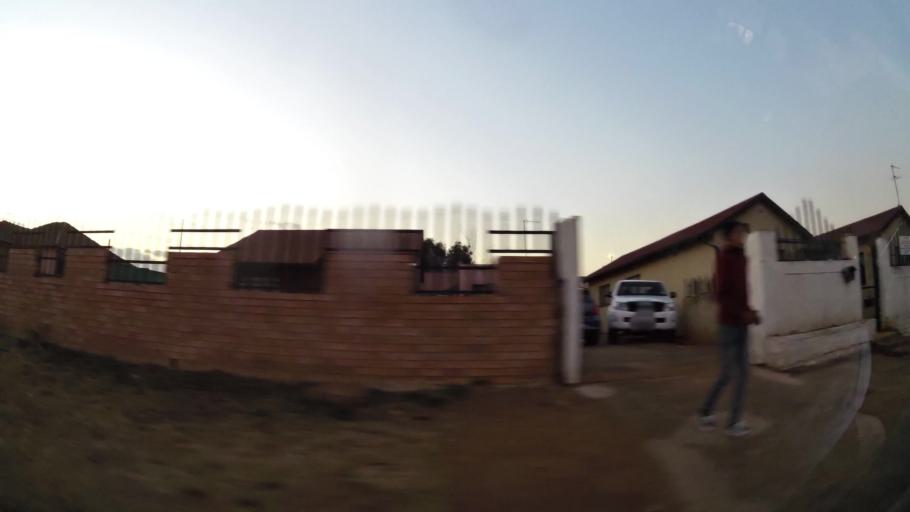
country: ZA
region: Gauteng
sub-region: West Rand District Municipality
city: Randfontein
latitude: -26.2067
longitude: 27.7113
